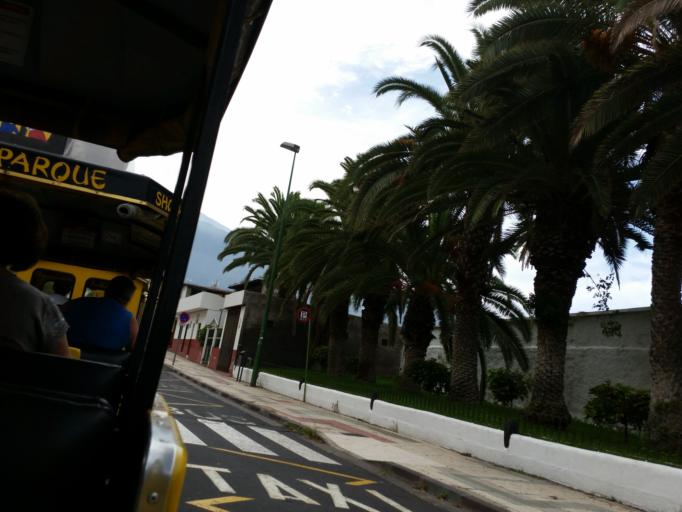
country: ES
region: Canary Islands
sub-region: Provincia de Santa Cruz de Tenerife
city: Puerto de la Cruz
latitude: 28.4141
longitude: -16.5570
